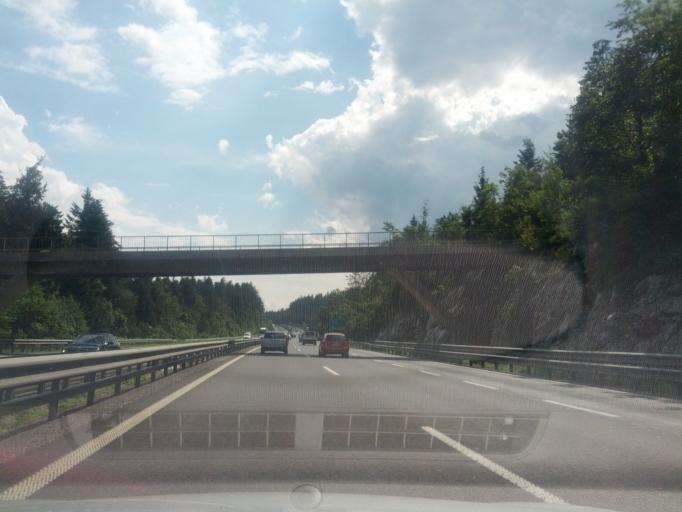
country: SI
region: Logatec
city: Logatec
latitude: 45.9196
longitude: 14.2660
